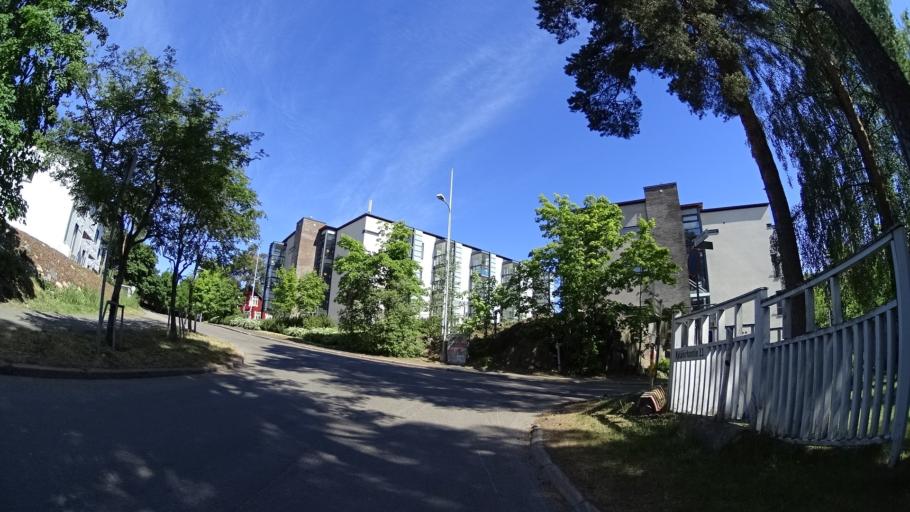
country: FI
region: Uusimaa
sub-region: Helsinki
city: Teekkarikylae
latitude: 60.2239
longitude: 24.8434
